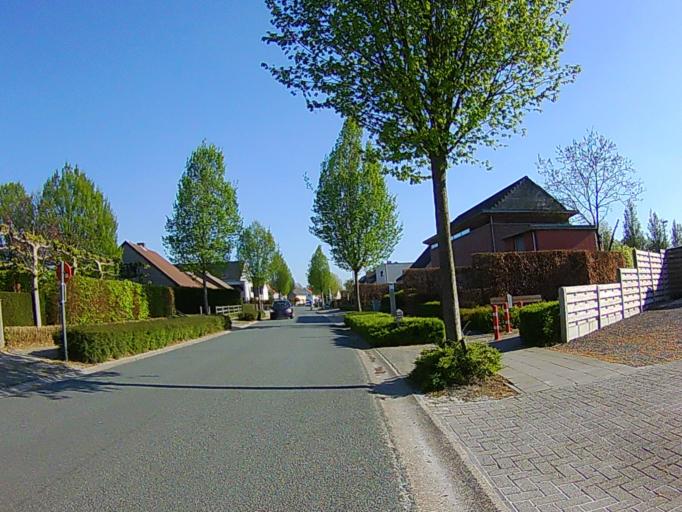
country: BE
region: Flanders
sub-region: Provincie Antwerpen
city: Hoogstraten
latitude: 51.3931
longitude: 4.7637
